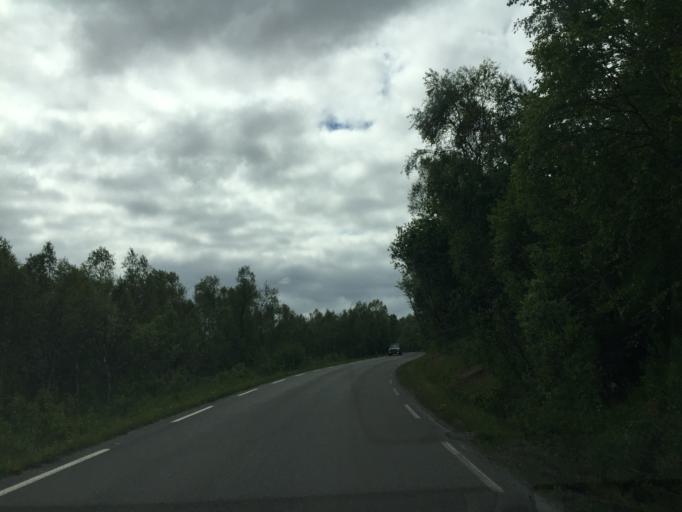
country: NO
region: Nordland
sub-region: Bodo
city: Loding
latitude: 67.3013
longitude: 14.6208
